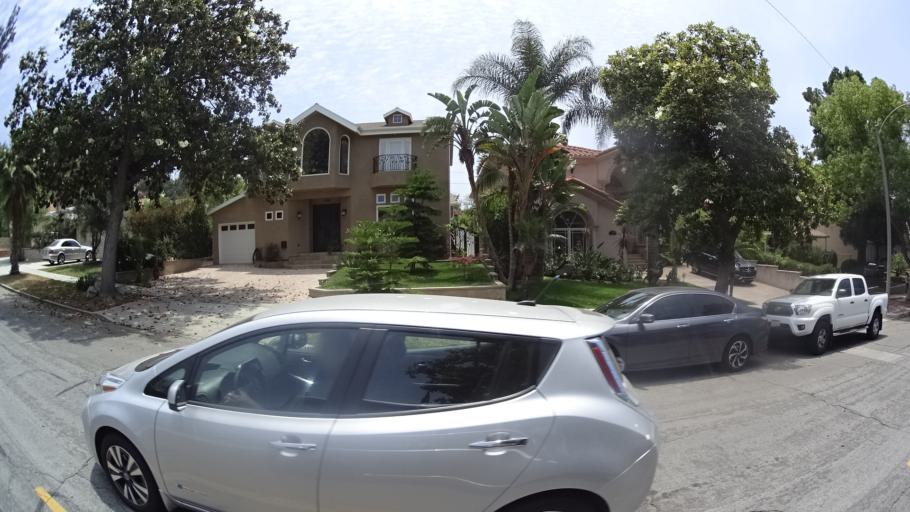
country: US
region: California
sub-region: Los Angeles County
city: Burbank
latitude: 34.1941
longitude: -118.3001
